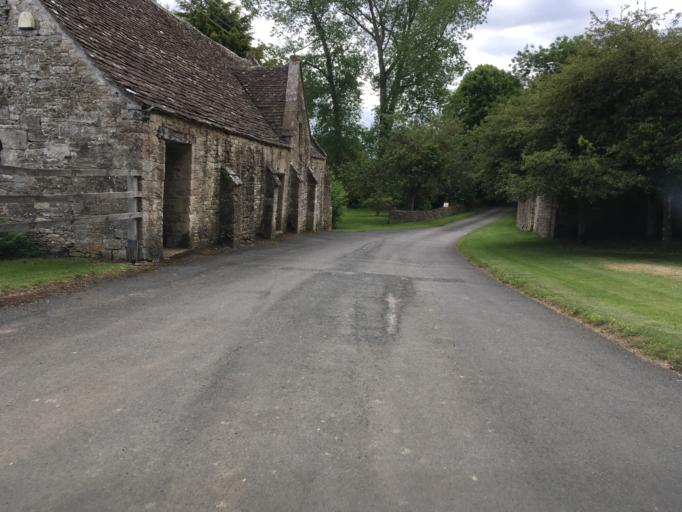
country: GB
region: England
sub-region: Gloucestershire
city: Tetbury
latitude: 51.6440
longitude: -2.2004
